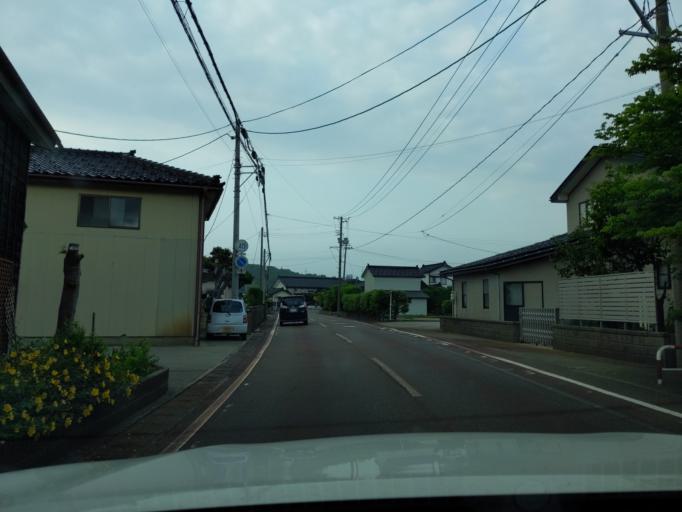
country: JP
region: Niigata
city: Kashiwazaki
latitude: 37.3891
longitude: 138.5856
